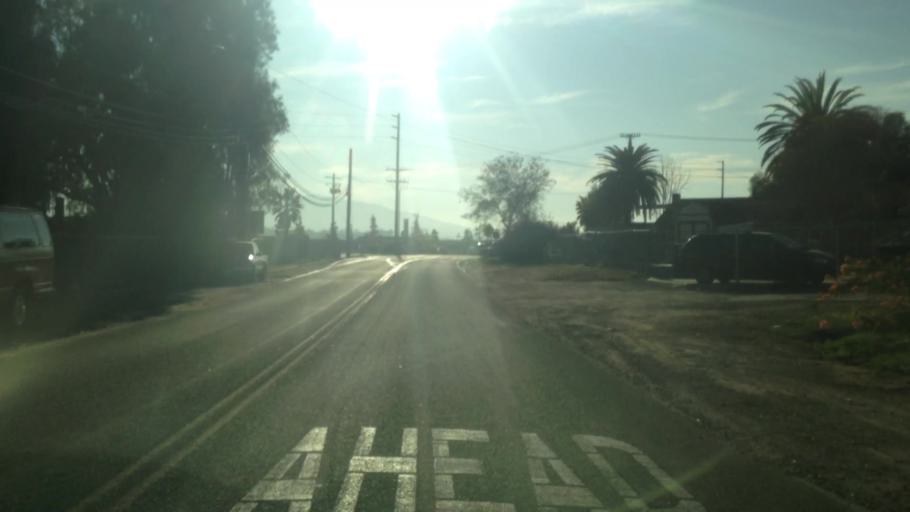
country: US
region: California
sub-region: Riverside County
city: Norco
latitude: 33.9655
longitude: -117.5395
